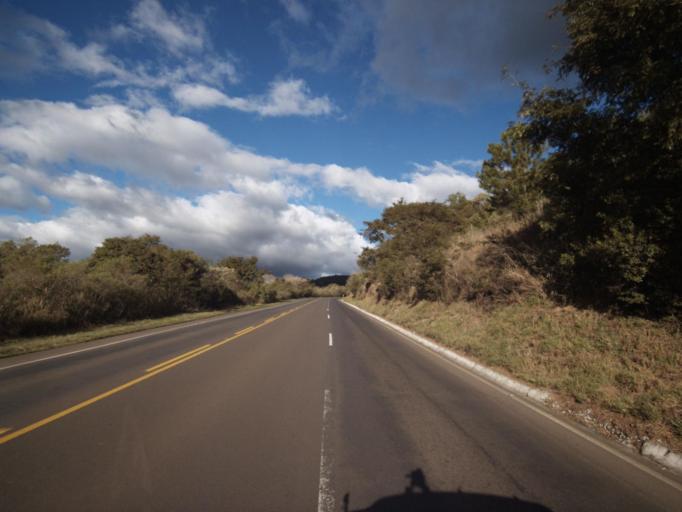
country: BR
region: Santa Catarina
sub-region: Joacaba
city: Joacaba
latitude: -27.2921
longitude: -51.4142
